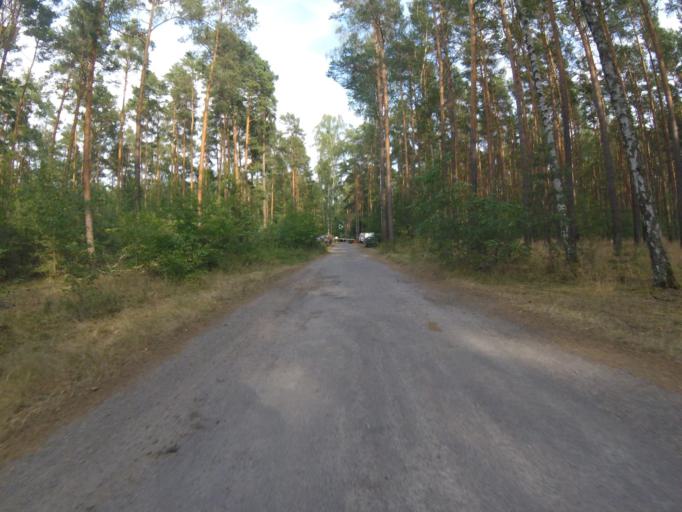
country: DE
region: Brandenburg
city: Gross Koris
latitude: 52.2126
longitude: 13.7429
